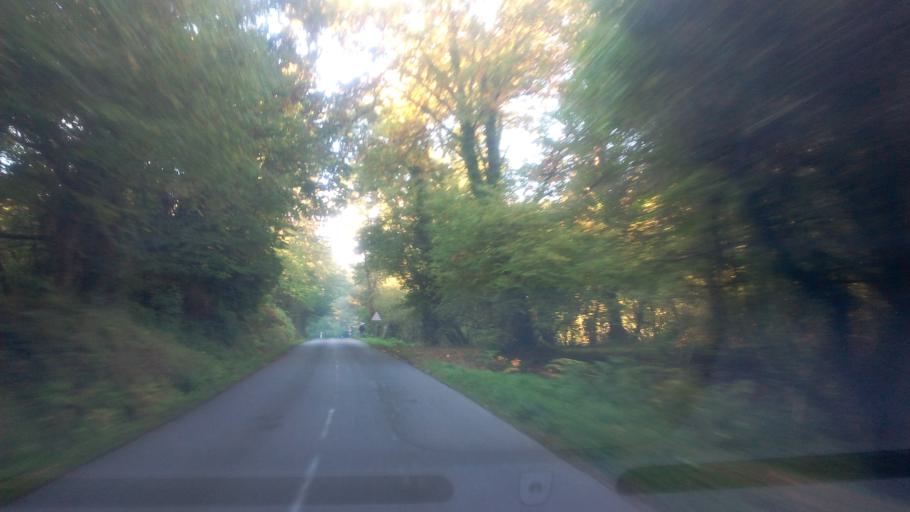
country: FR
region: Brittany
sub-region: Departement du Morbihan
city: Saint-Jean-la-Poterie
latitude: 47.6421
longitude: -2.1210
